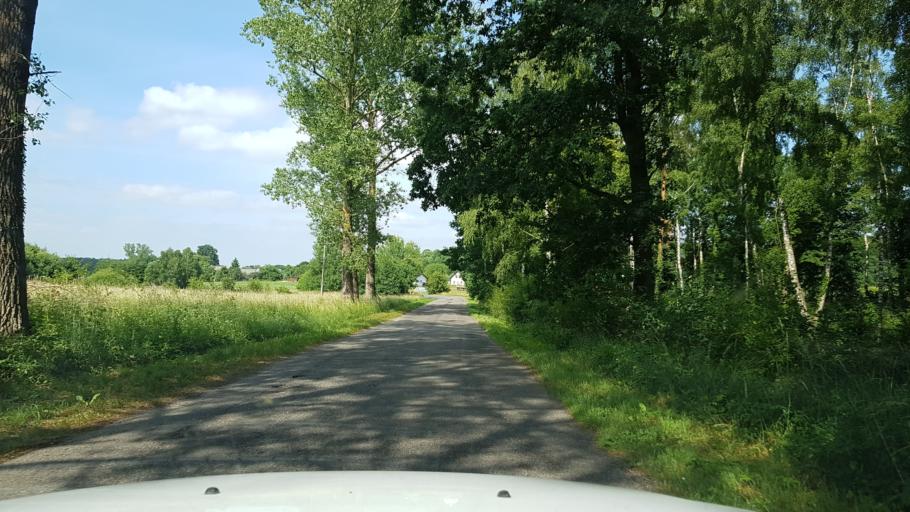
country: PL
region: West Pomeranian Voivodeship
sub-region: Powiat goleniowski
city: Osina
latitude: 53.5989
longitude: 15.0032
